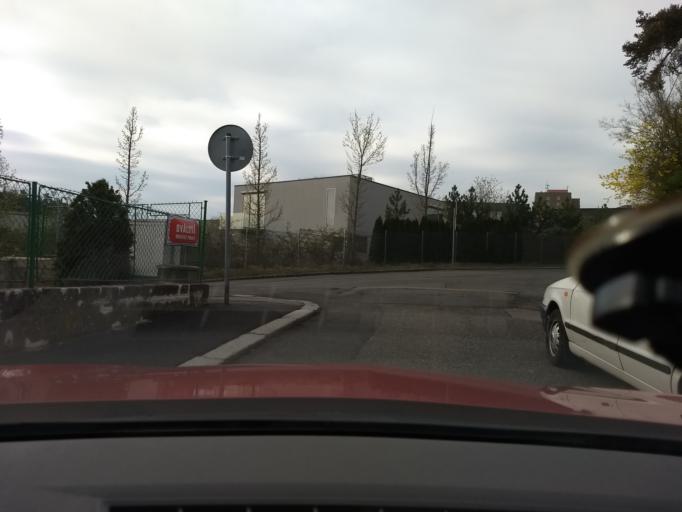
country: CZ
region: Central Bohemia
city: Horomerice
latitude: 50.1003
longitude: 14.3483
